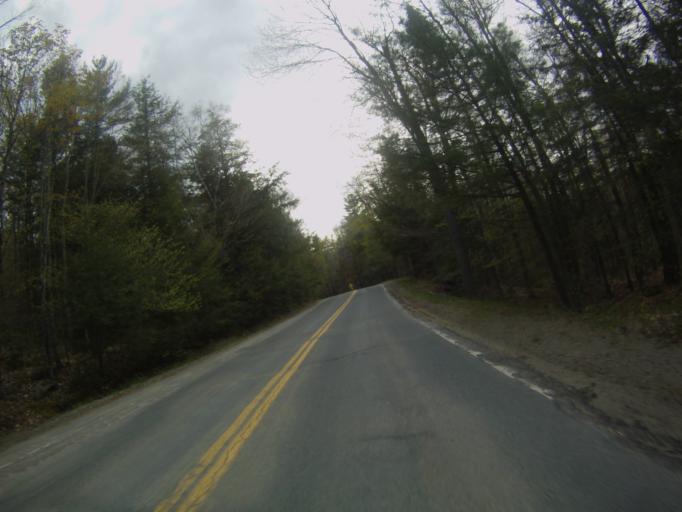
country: US
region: New York
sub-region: Warren County
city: Warrensburg
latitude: 43.8259
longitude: -73.9045
